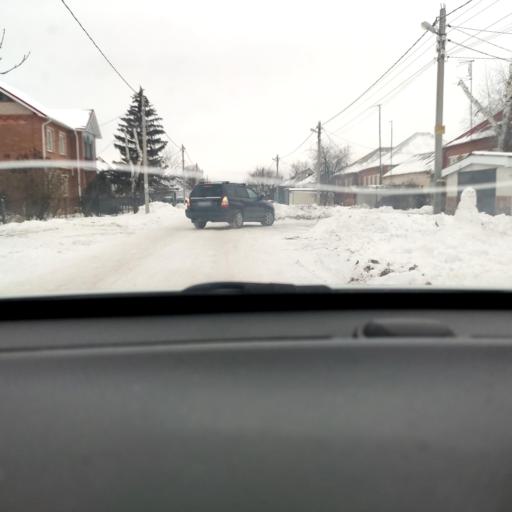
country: RU
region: Voronezj
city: Somovo
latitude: 51.7515
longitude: 39.3409
